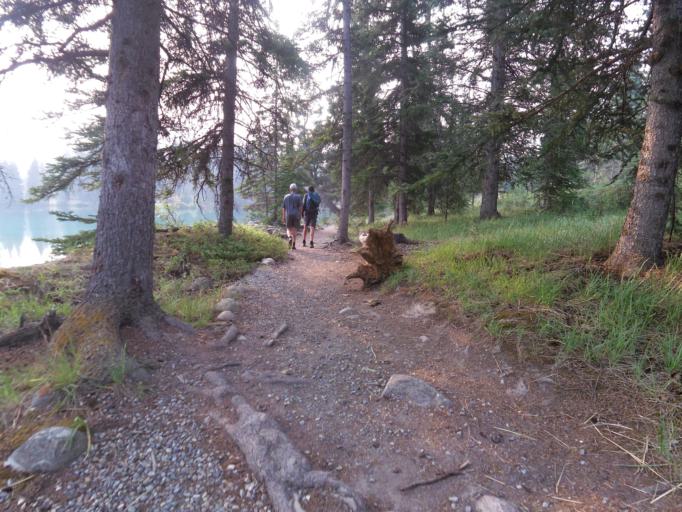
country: CA
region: Alberta
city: Jasper Park Lodge
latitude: 52.8791
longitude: -118.0618
